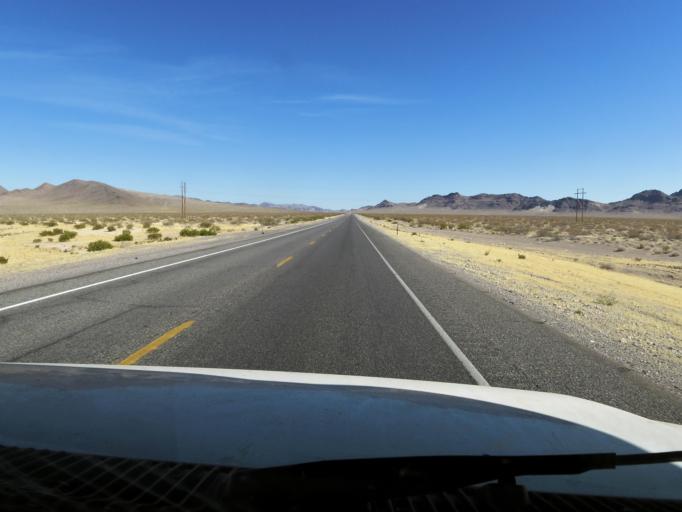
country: US
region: Nevada
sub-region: Nye County
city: Beatty
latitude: 36.6387
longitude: -116.3796
